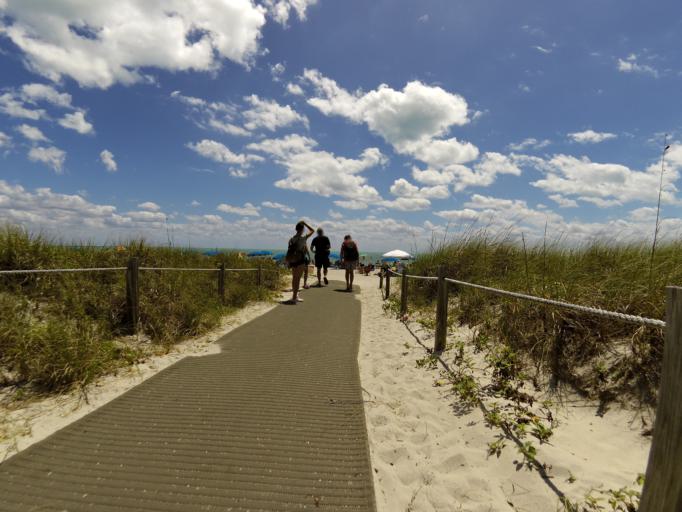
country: US
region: Florida
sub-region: Miami-Dade County
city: Key Biscayne
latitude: 25.6689
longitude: -80.1548
